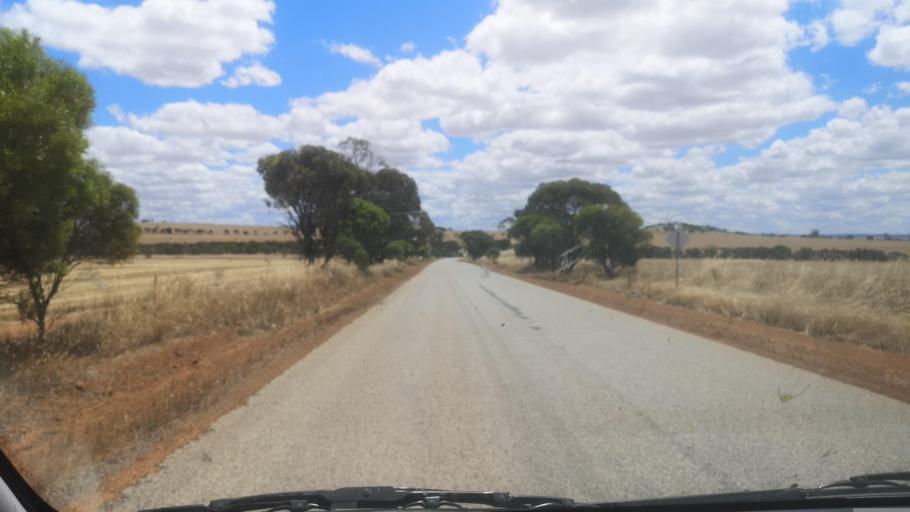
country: AU
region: Western Australia
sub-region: Cunderdin
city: Cunderdin
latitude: -32.0755
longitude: 117.5484
